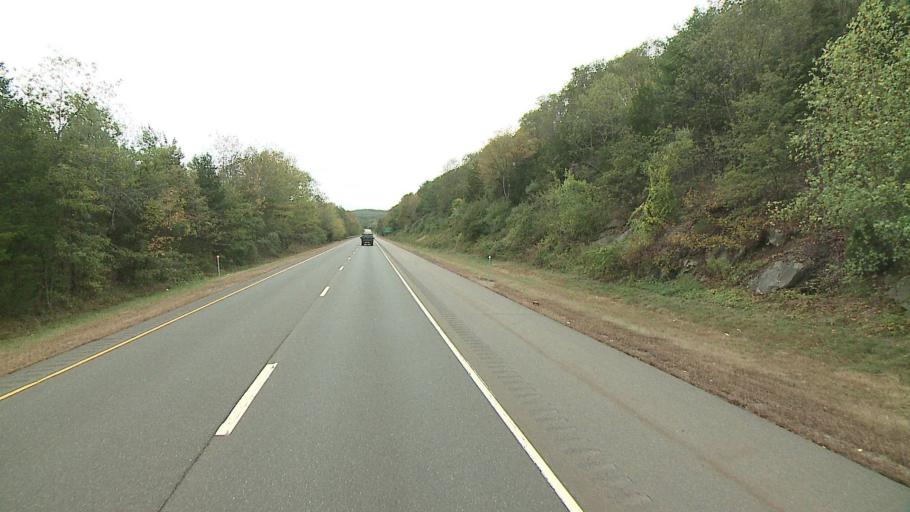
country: US
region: Connecticut
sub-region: Middlesex County
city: Essex Village
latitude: 41.3428
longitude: -72.3984
